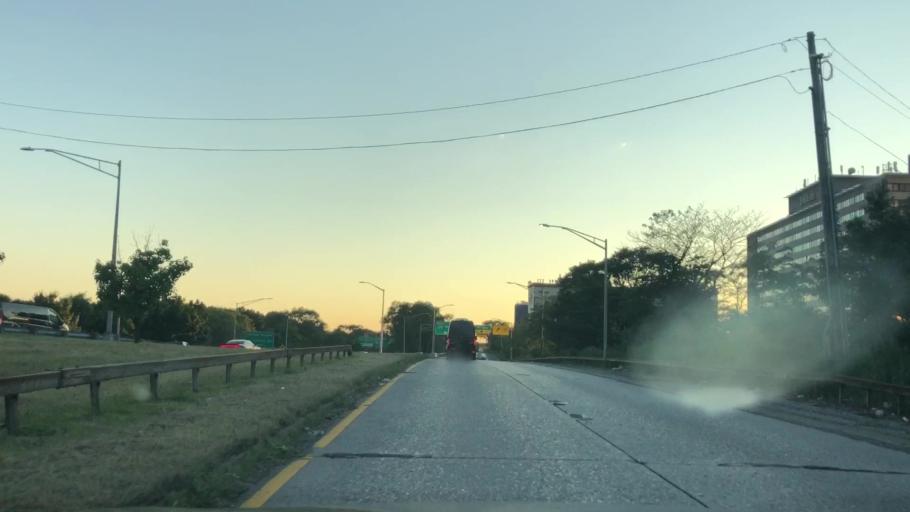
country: US
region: New York
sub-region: Queens County
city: Jamaica
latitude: 40.6668
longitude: -73.7938
